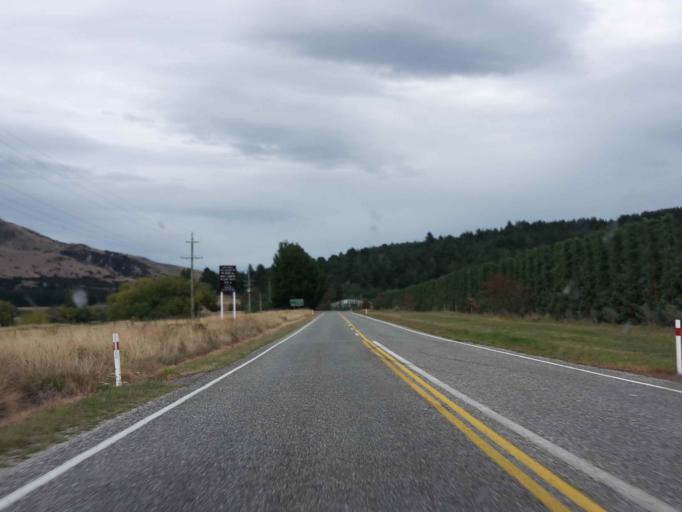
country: NZ
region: Otago
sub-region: Queenstown-Lakes District
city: Wanaka
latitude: -44.7354
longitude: 169.1352
